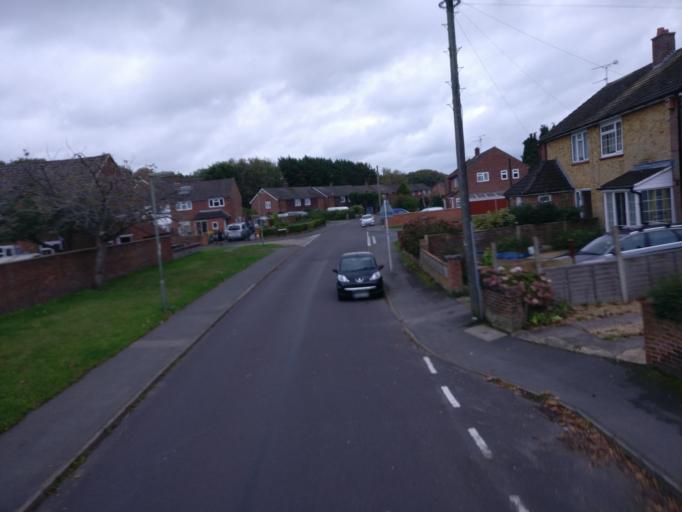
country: GB
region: England
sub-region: Surrey
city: Camberley
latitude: 51.3529
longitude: -0.7190
